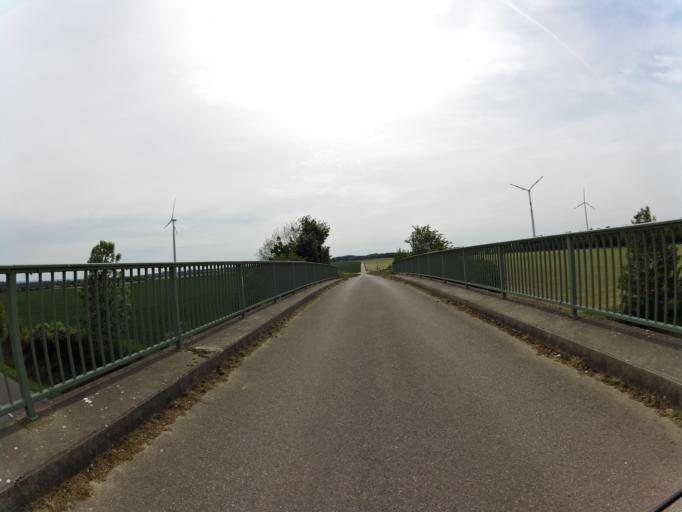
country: DE
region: North Rhine-Westphalia
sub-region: Regierungsbezirk Koln
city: Wurselen
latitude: 50.8404
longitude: 6.1537
